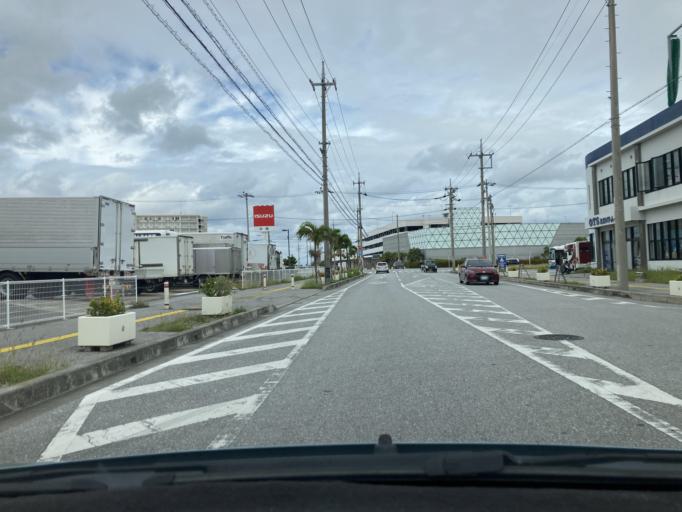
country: JP
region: Okinawa
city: Itoman
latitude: 26.1585
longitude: 127.6543
